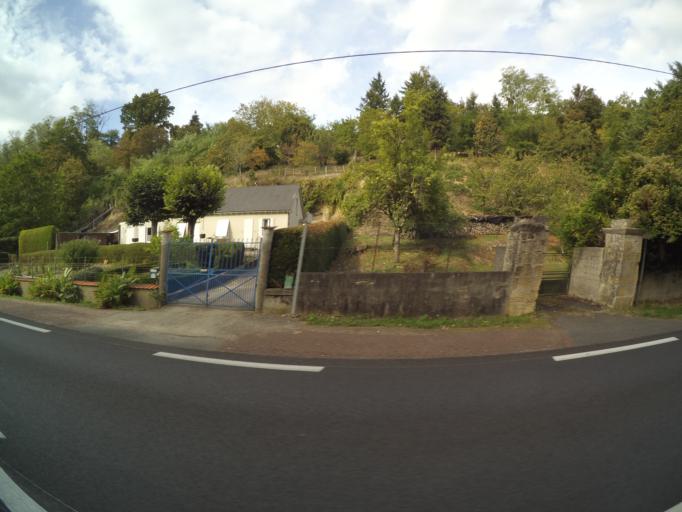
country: FR
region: Centre
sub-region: Departement d'Indre-et-Loire
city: Langeais
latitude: 47.3149
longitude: 0.3797
